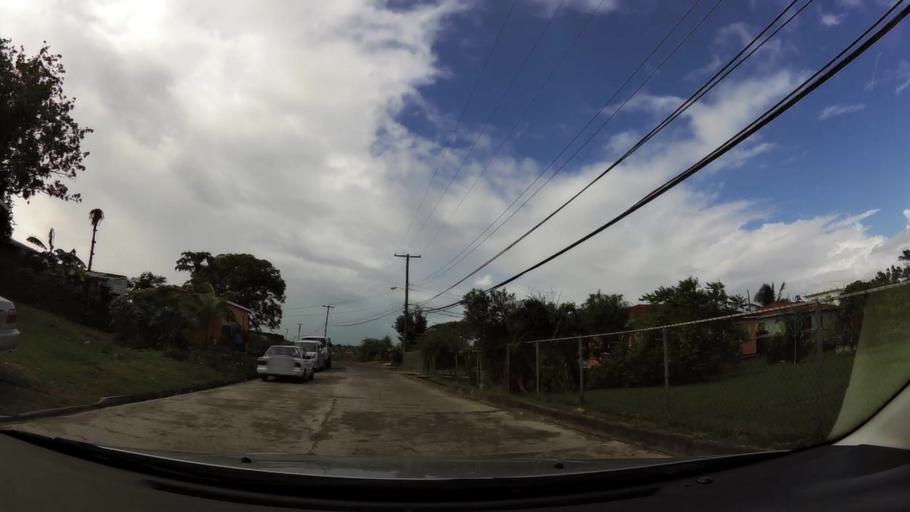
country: AG
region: Saint George
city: Piggotts
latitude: 17.1110
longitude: -61.8150
